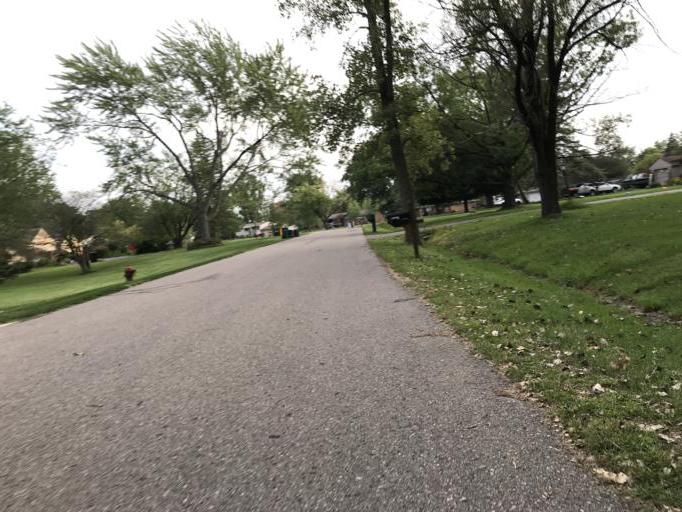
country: US
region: Michigan
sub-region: Oakland County
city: Farmington
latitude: 42.4736
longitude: -83.3513
